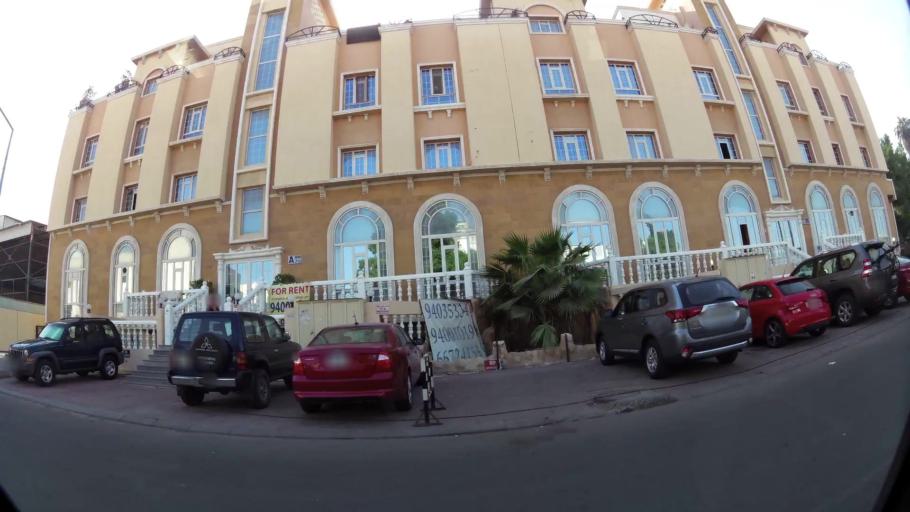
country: KW
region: Muhafazat Hawalli
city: Salwa
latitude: 29.2915
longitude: 48.0727
